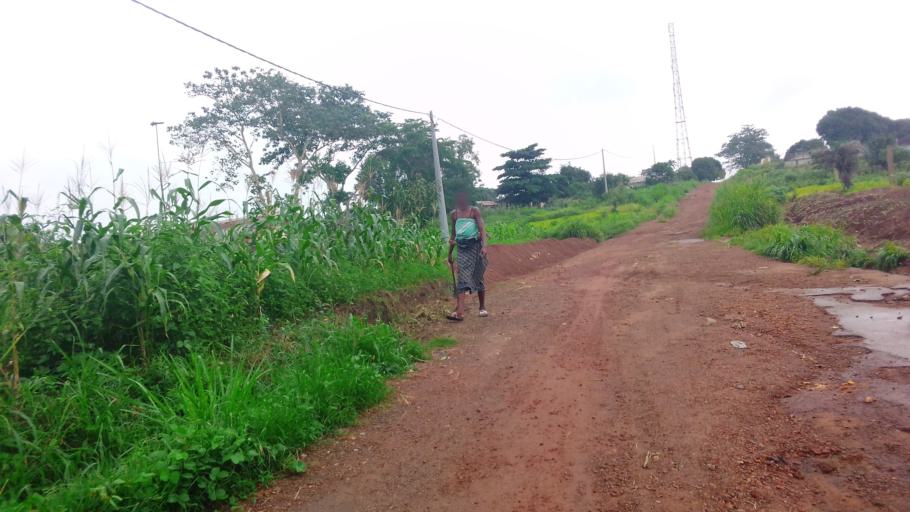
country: SL
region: Northern Province
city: Lunsar
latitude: 8.6859
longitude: -12.5262
